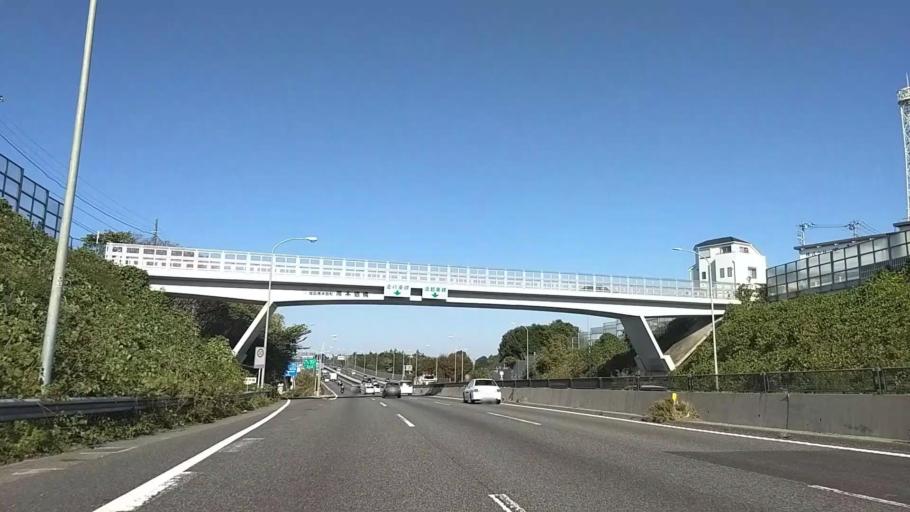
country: JP
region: Kanagawa
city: Minami-rinkan
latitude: 35.4602
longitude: 139.5447
